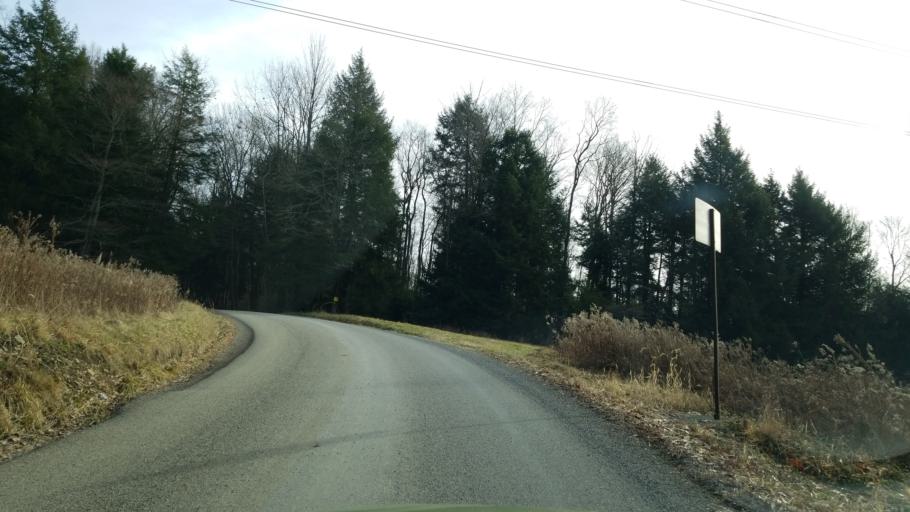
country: US
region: Pennsylvania
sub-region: Indiana County
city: Johnsonburg
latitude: 40.9397
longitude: -78.8911
